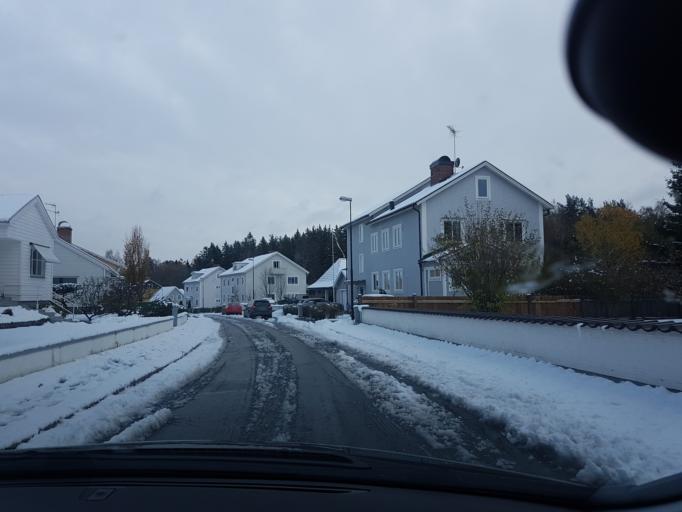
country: SE
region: Joenkoeping
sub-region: Vetlanda Kommun
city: Vetlanda
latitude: 57.4217
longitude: 15.0915
